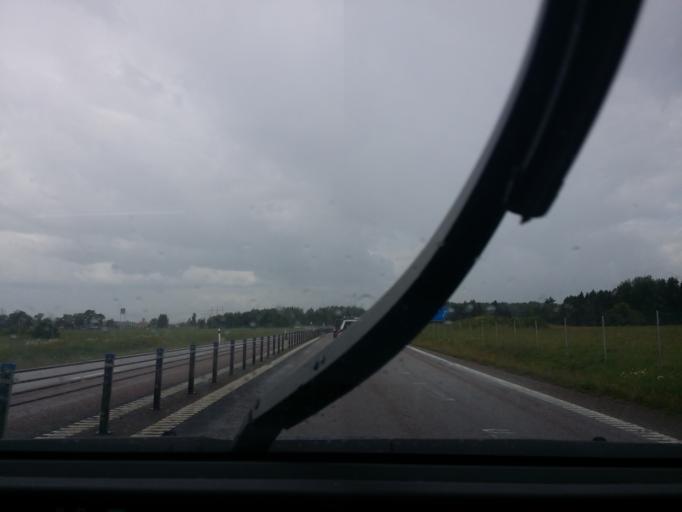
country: SE
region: Vaestmanland
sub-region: Hallstahammars Kommun
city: Kolback
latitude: 59.5906
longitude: 16.2586
